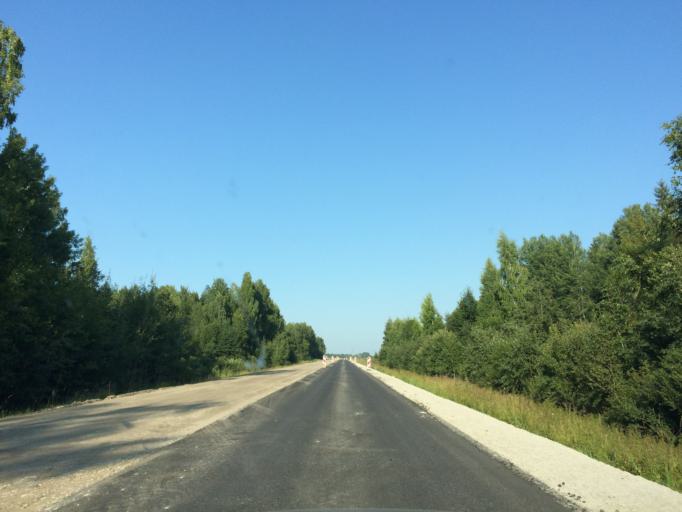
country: LV
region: Rezekne
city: Rezekne
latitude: 56.5162
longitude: 27.4941
